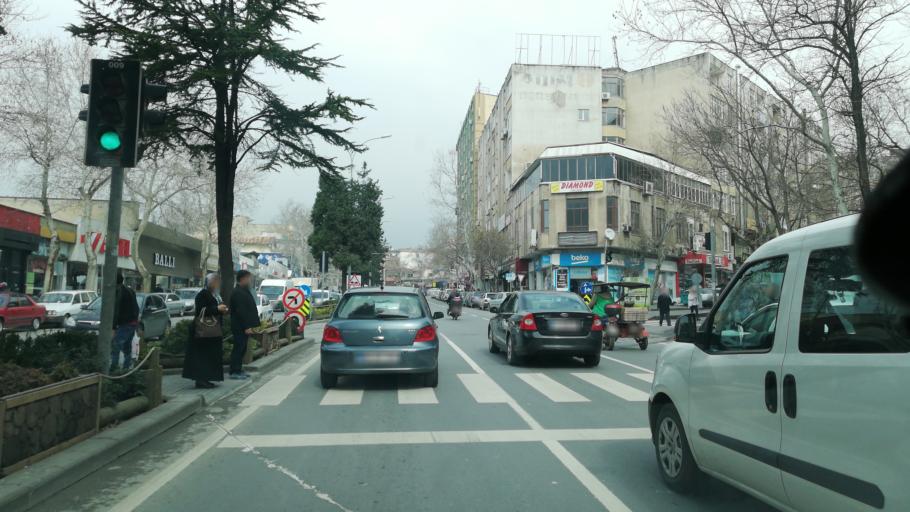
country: TR
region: Kahramanmaras
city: Kahramanmaras
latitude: 37.5798
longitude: 36.9271
